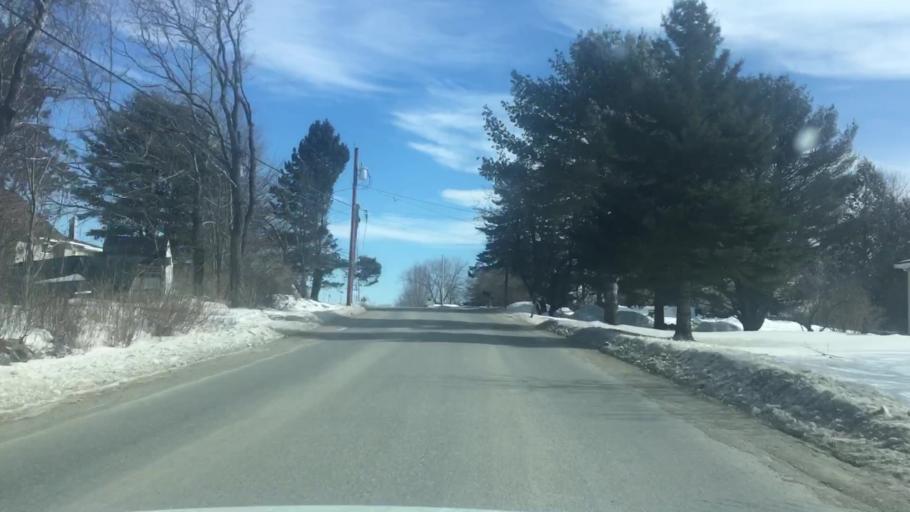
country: US
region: Maine
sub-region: Penobscot County
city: Eddington
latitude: 44.7982
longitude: -68.6760
